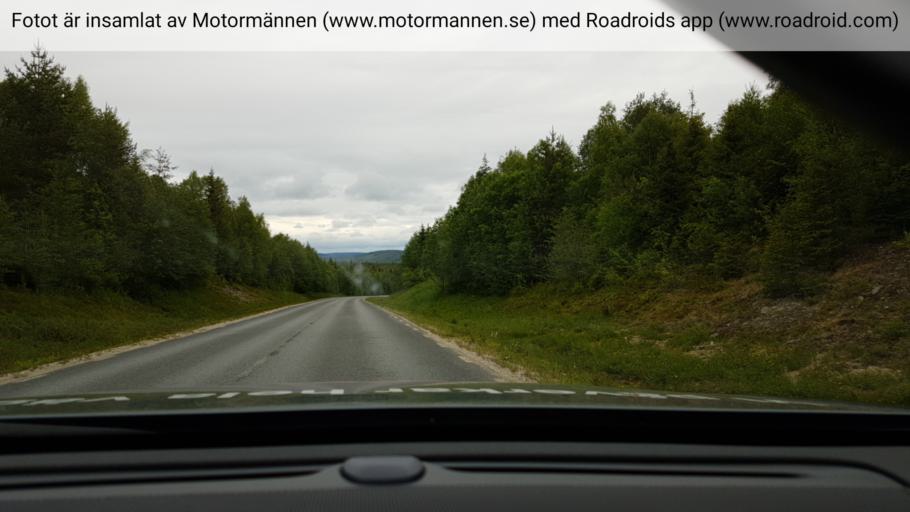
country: SE
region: Vaesterbotten
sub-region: Lycksele Kommun
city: Lycksele
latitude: 64.4963
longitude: 18.2921
